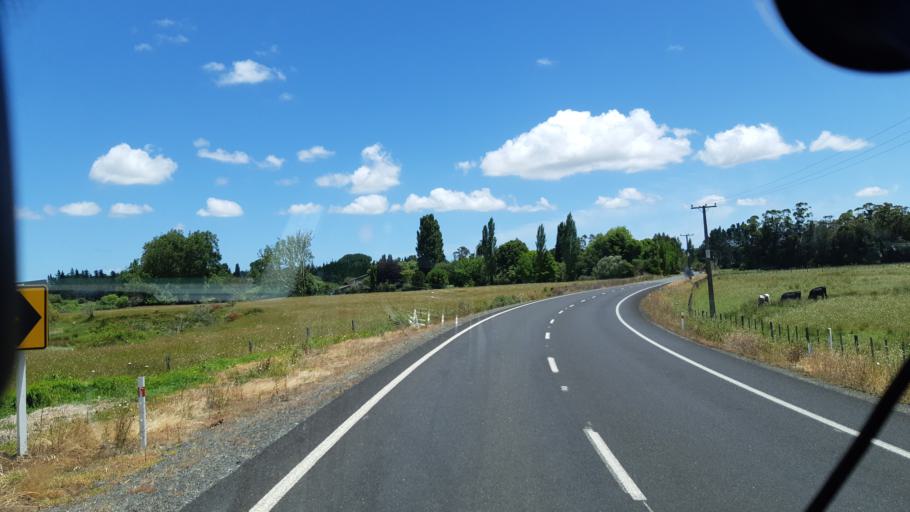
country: NZ
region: Northland
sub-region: Far North District
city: Kaitaia
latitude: -35.1372
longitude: 173.3561
